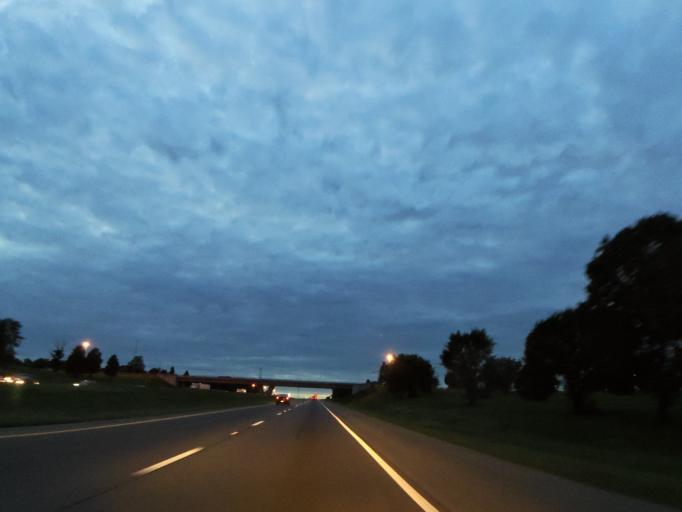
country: US
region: Tennessee
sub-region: Robertson County
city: Coopertown
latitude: 36.3474
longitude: -86.9293
